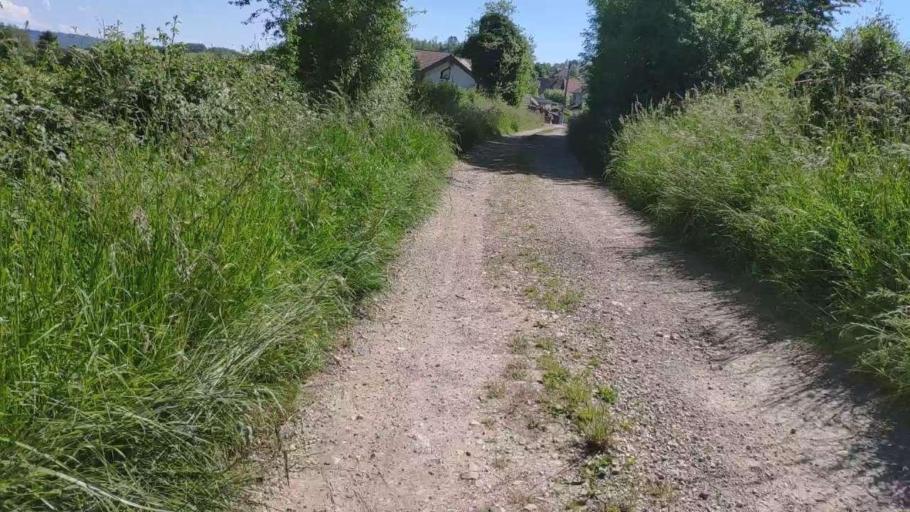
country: FR
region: Franche-Comte
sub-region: Departement du Jura
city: Perrigny
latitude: 46.7217
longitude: 5.5831
